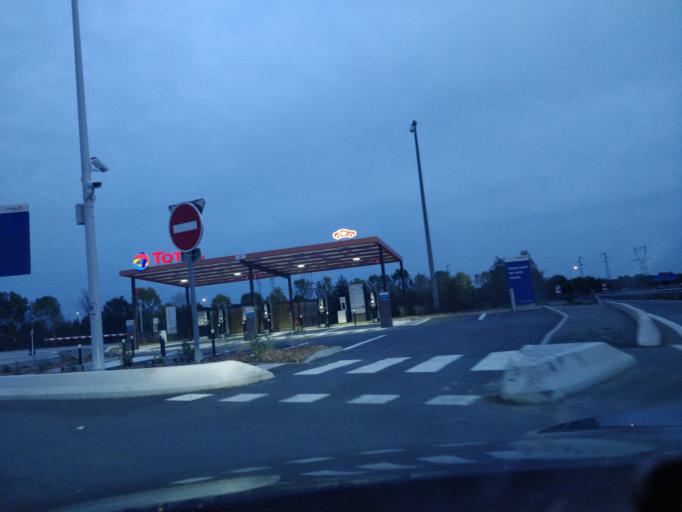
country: FR
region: Ile-de-France
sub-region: Departement de l'Essonne
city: Fontenay-les-Briis
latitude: 48.6356
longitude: 2.1454
